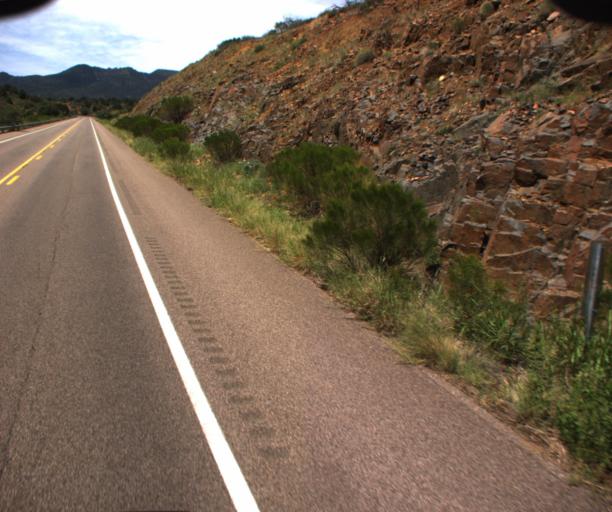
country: US
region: Arizona
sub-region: Gila County
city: Globe
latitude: 33.5515
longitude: -110.6832
